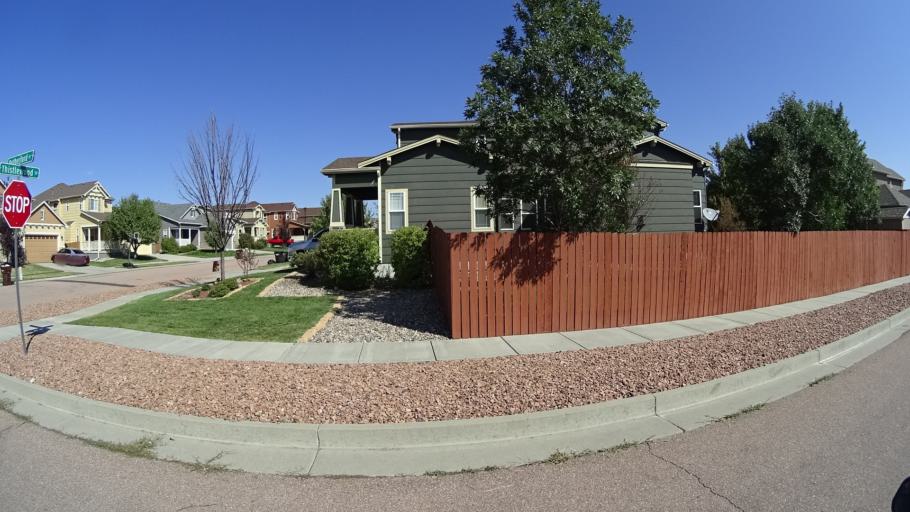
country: US
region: Colorado
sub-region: El Paso County
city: Cimarron Hills
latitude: 38.9278
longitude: -104.7040
